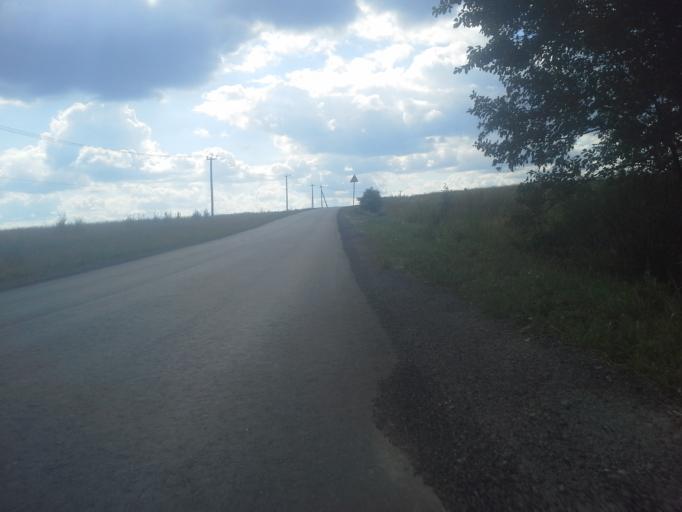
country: RU
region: Moskovskaya
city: Kievskij
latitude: 55.3151
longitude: 37.0371
